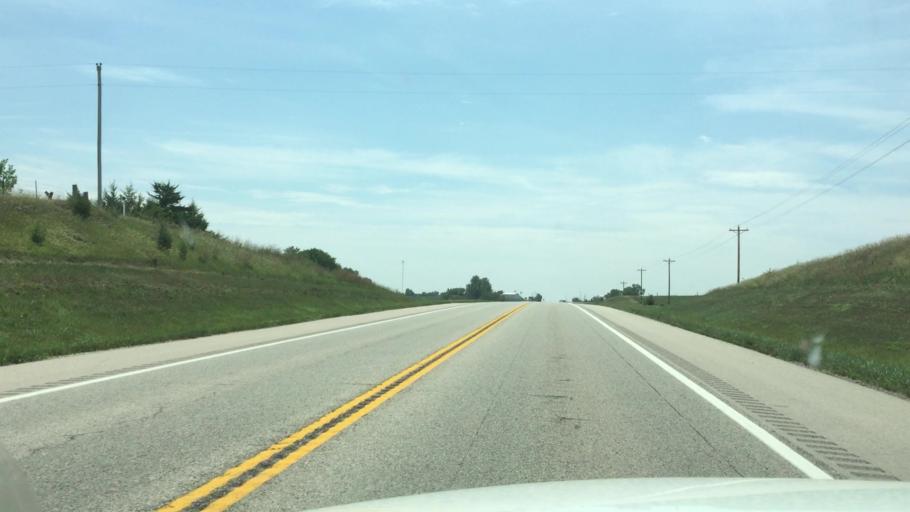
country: US
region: Kansas
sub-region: Jackson County
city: Holton
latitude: 39.6244
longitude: -95.7311
